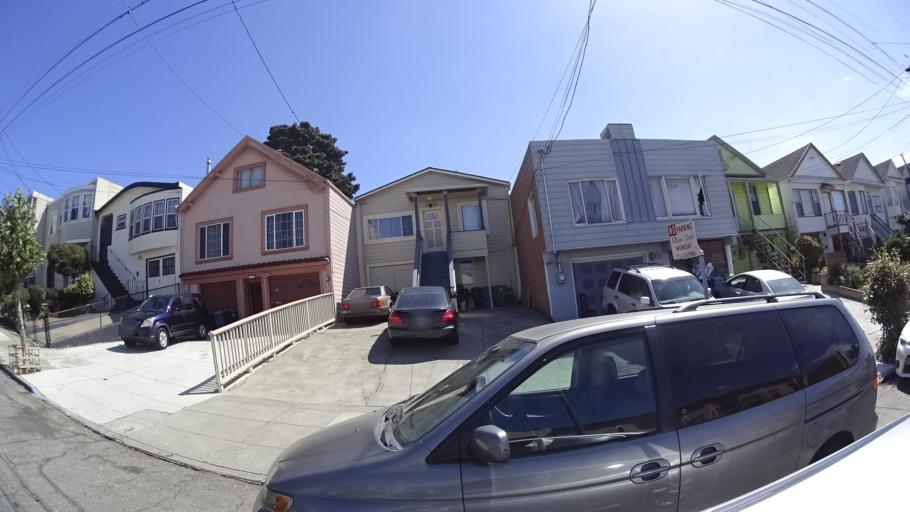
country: US
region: California
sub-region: San Mateo County
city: Daly City
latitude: 37.7244
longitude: -122.4275
